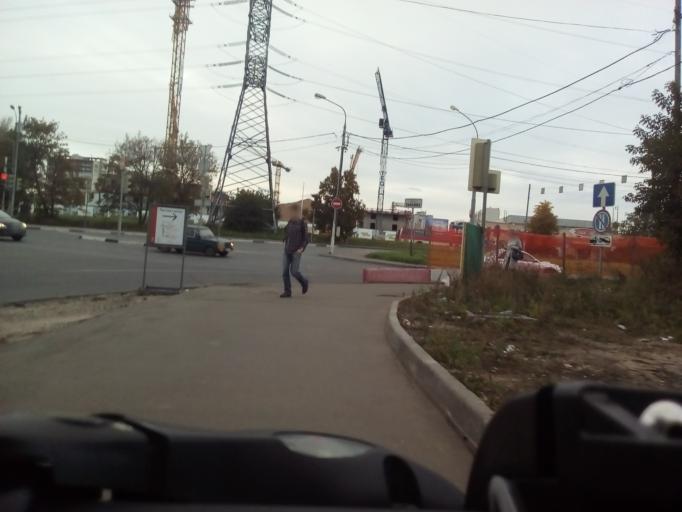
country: RU
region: Moscow
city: Sviblovo
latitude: 55.8458
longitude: 37.6362
